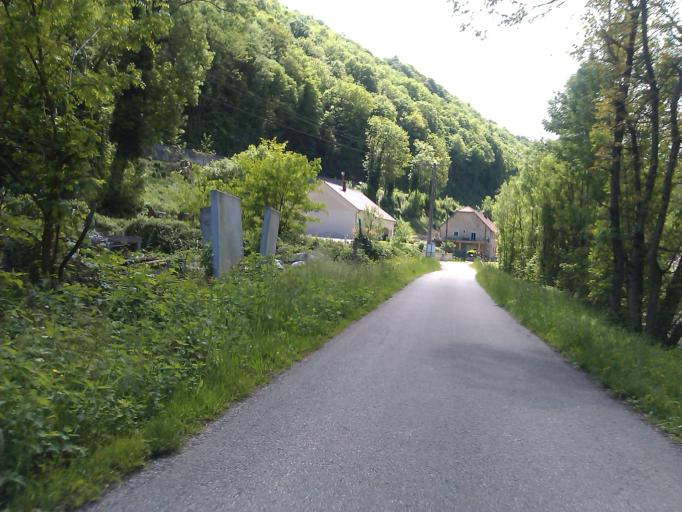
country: FR
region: Franche-Comte
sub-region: Departement du Doubs
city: Beure
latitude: 47.2020
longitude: 5.9935
